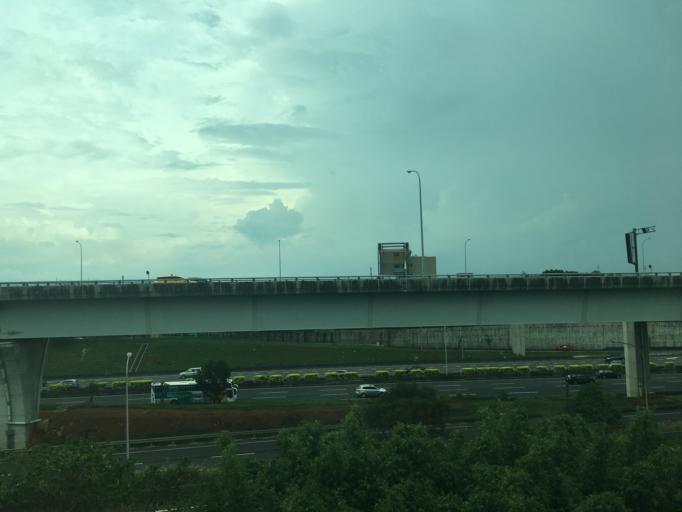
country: TW
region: Taiwan
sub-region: Taoyuan
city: Taoyuan
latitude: 25.0663
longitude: 121.3531
